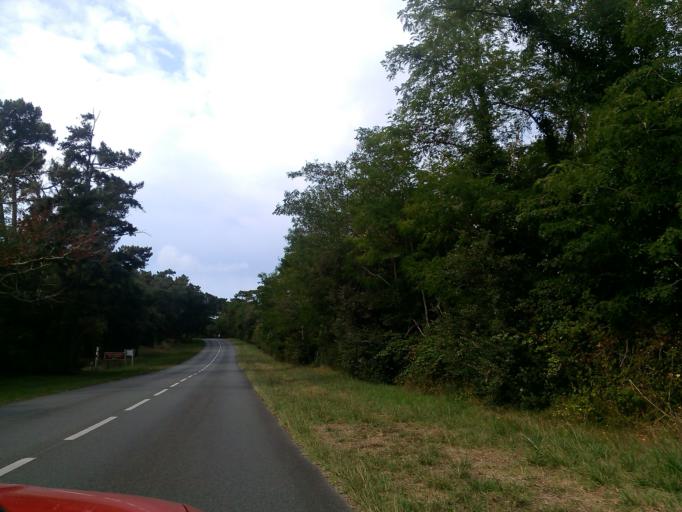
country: FR
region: Poitou-Charentes
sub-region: Departement de la Charente-Maritime
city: La Tremblade
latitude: 45.7917
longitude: -1.1809
